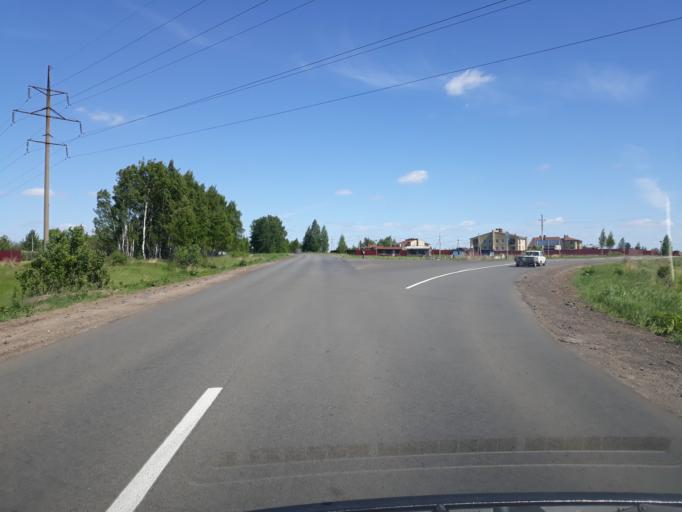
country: RU
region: Jaroslavl
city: Yaroslavl
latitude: 57.6693
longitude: 40.0225
